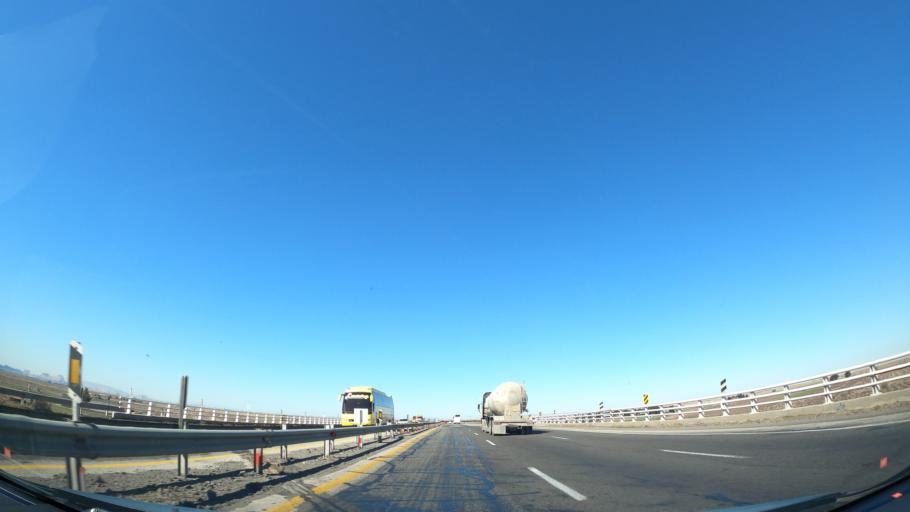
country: IR
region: Qom
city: Qom
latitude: 34.5264
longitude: 51.0268
